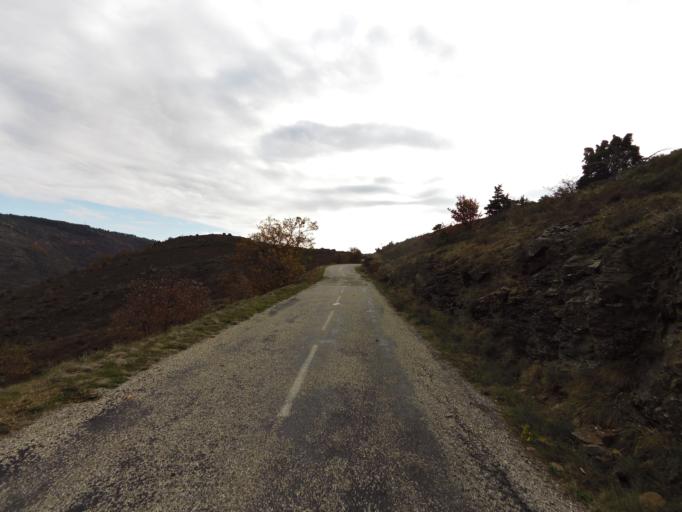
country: FR
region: Rhone-Alpes
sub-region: Departement de l'Ardeche
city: Les Vans
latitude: 44.5116
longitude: 4.0570
